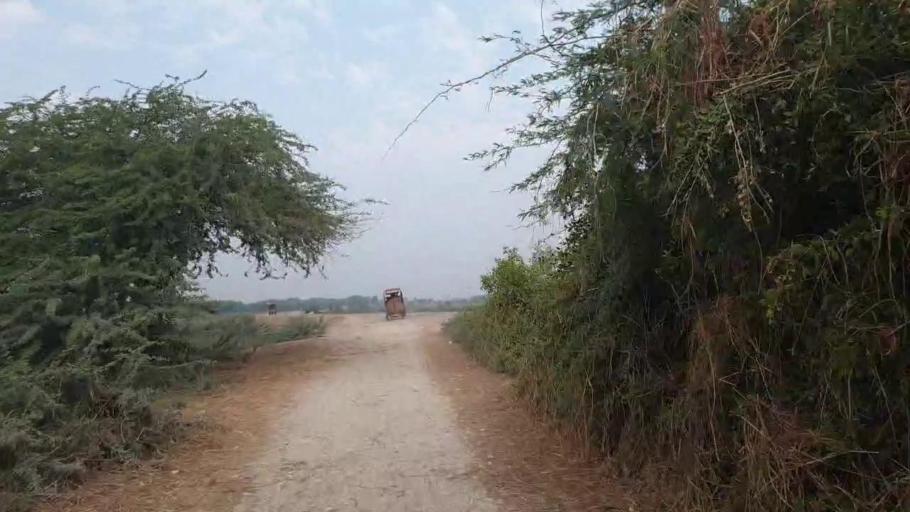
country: PK
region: Sindh
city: Talhar
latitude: 24.8427
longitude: 68.8727
